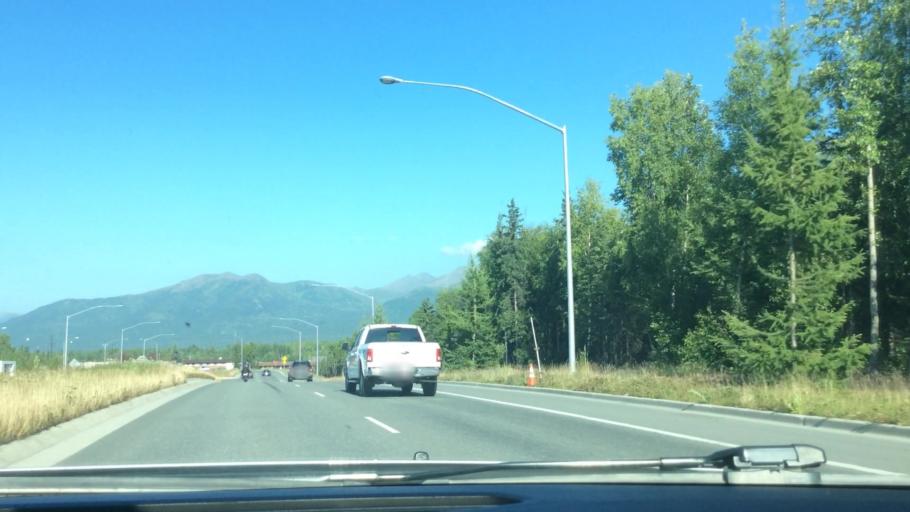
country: US
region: Alaska
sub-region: Anchorage Municipality
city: Anchorage
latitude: 61.1785
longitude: -149.7849
